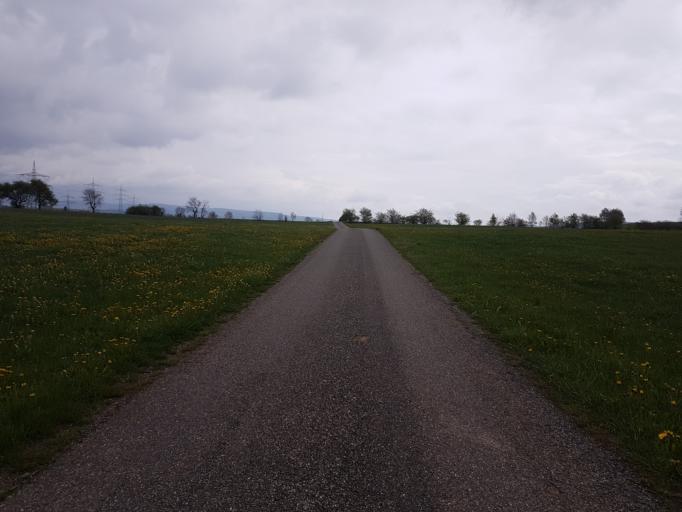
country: DE
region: Baden-Wuerttemberg
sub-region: Freiburg Region
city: Hufingen
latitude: 47.9106
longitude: 8.5249
